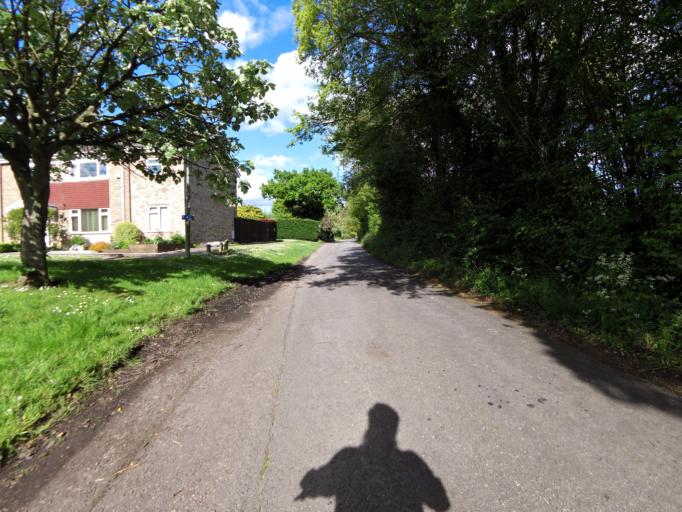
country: GB
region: England
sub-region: Suffolk
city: Woolpit
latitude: 52.2235
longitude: 0.8833
